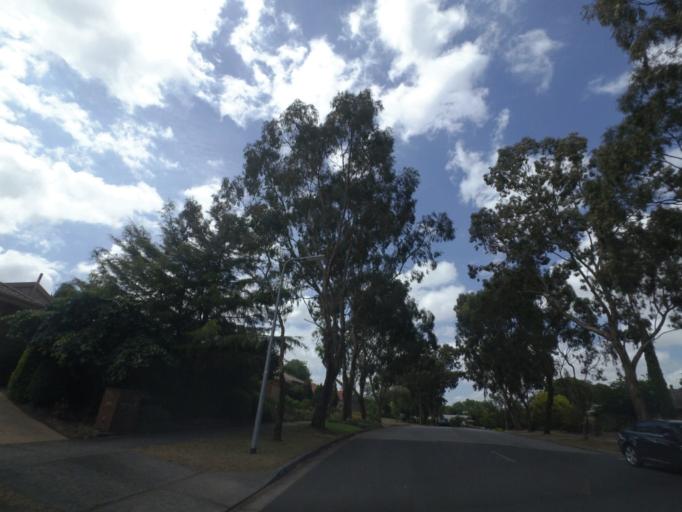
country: AU
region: Victoria
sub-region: Yarra Ranges
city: Lilydale
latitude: -37.7749
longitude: 145.3442
